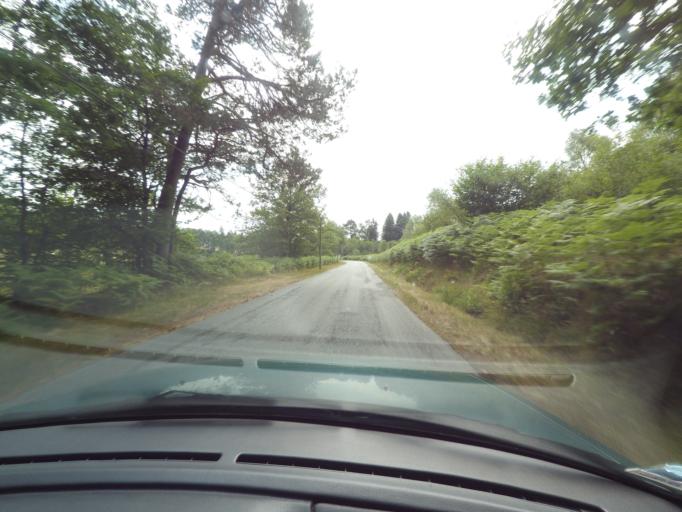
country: FR
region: Limousin
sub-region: Departement de la Correze
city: Bugeat
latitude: 45.7386
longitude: 1.9763
